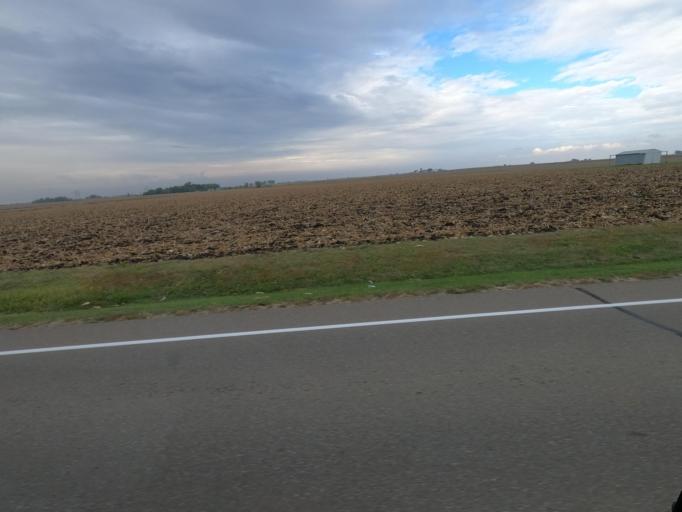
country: US
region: Iowa
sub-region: Henry County
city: Mount Pleasant
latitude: 40.7846
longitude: -91.6373
